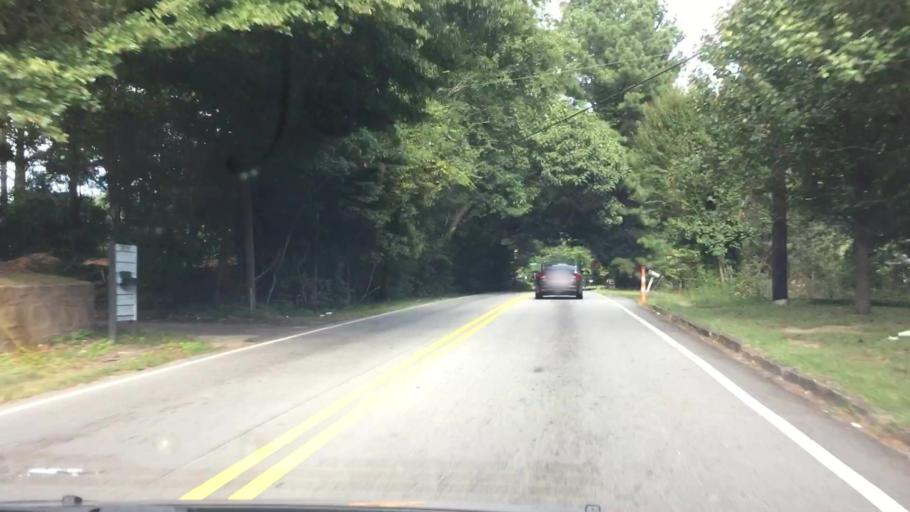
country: US
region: Georgia
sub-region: Clayton County
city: Conley
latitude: 33.6605
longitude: -84.2993
